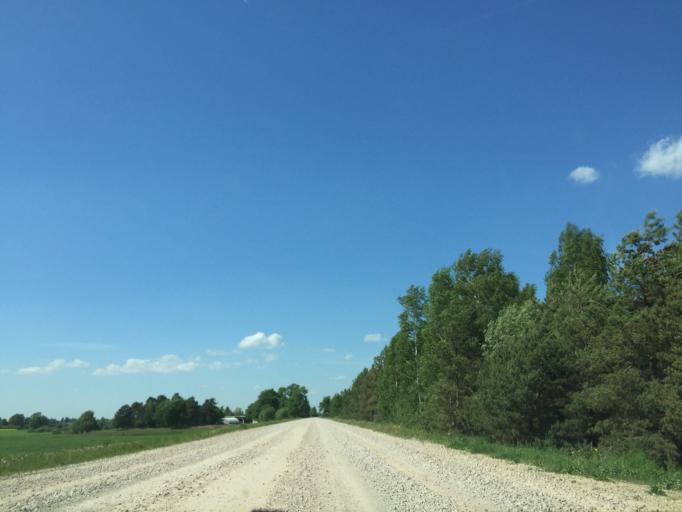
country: LV
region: Rundales
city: Pilsrundale
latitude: 56.5434
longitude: 23.9919
